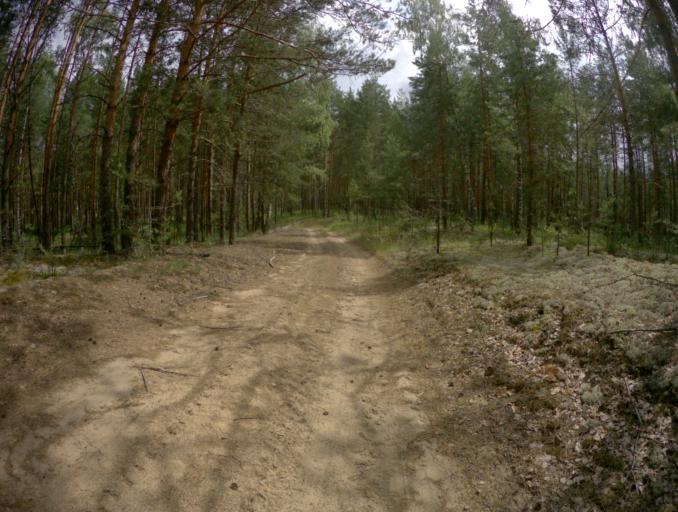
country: RU
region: Nizjnij Novgorod
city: Frolishchi
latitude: 56.3142
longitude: 42.6677
